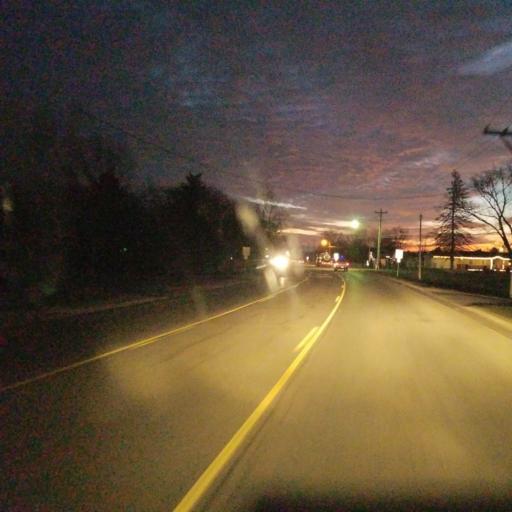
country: US
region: Illinois
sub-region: Peoria County
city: Hanna City
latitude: 40.6917
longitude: -89.7930
